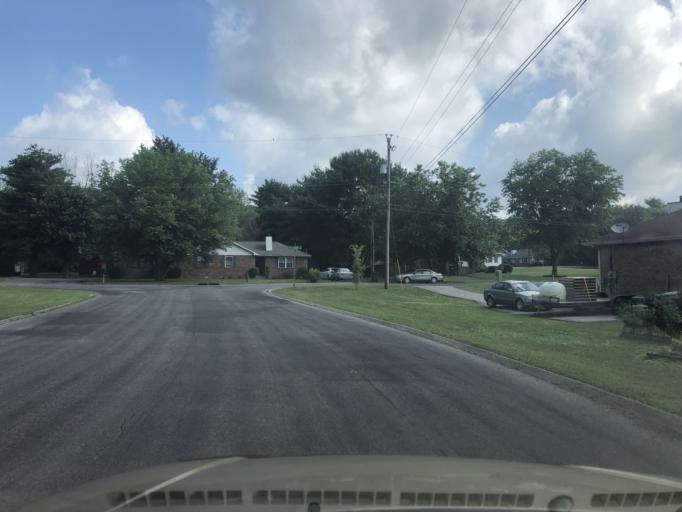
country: US
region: Tennessee
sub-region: Wilson County
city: Green Hill
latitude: 36.2345
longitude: -86.5921
